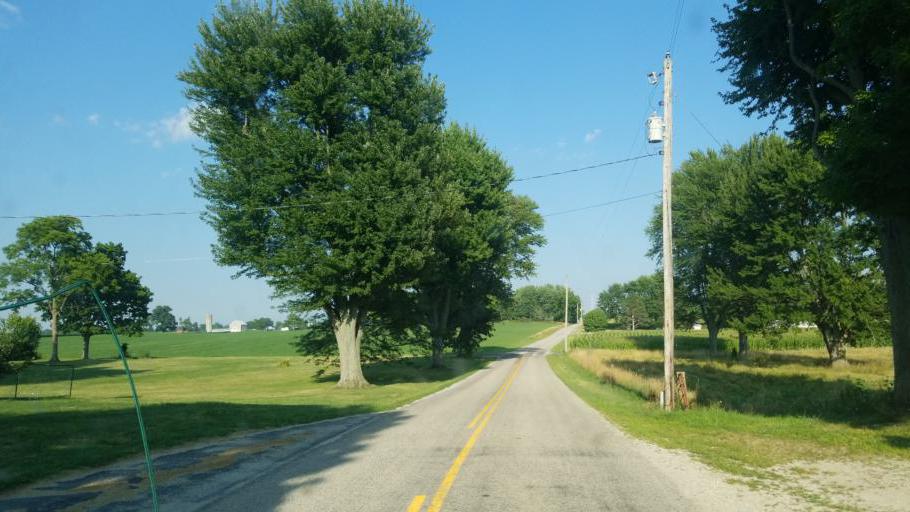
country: US
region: Ohio
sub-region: Crawford County
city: Bucyrus
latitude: 40.8543
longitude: -82.9175
